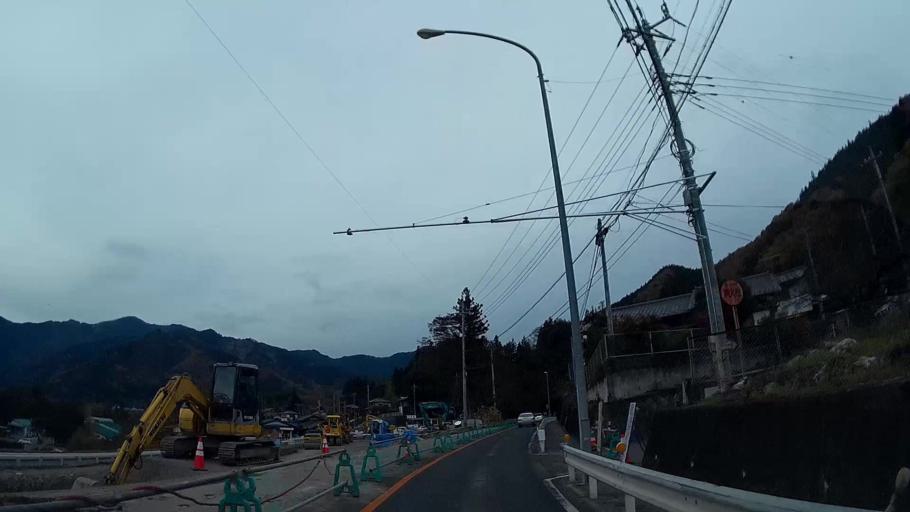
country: JP
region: Saitama
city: Chichibu
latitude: 35.9634
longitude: 138.9895
